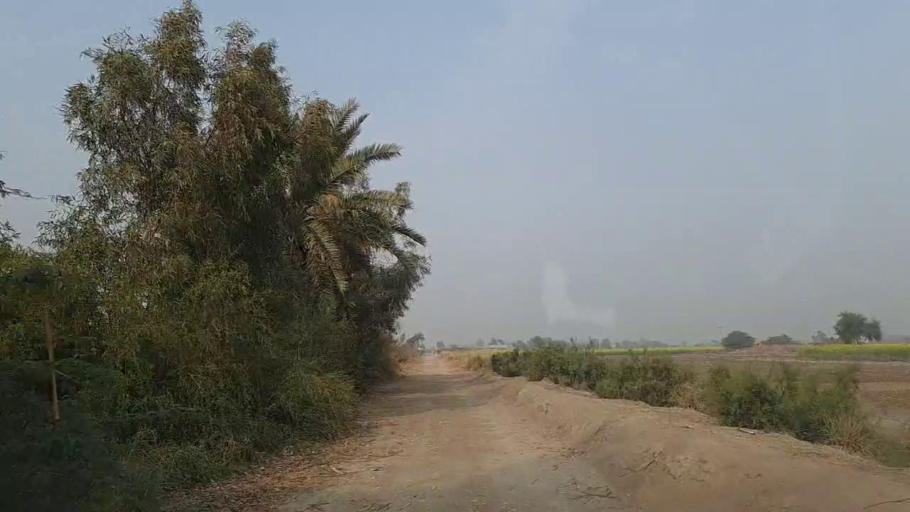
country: PK
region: Sindh
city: Sanghar
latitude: 26.1144
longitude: 68.8963
